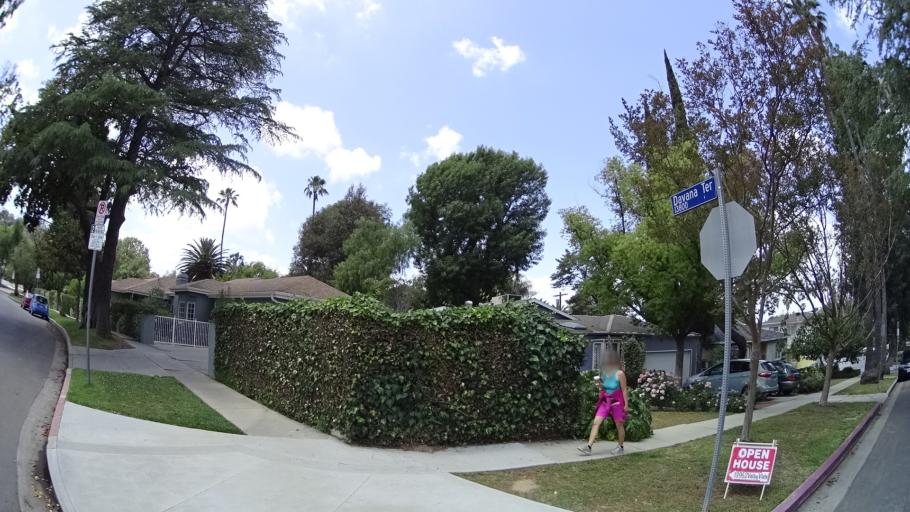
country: US
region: California
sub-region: Los Angeles County
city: Sherman Oaks
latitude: 34.1466
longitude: -118.4339
